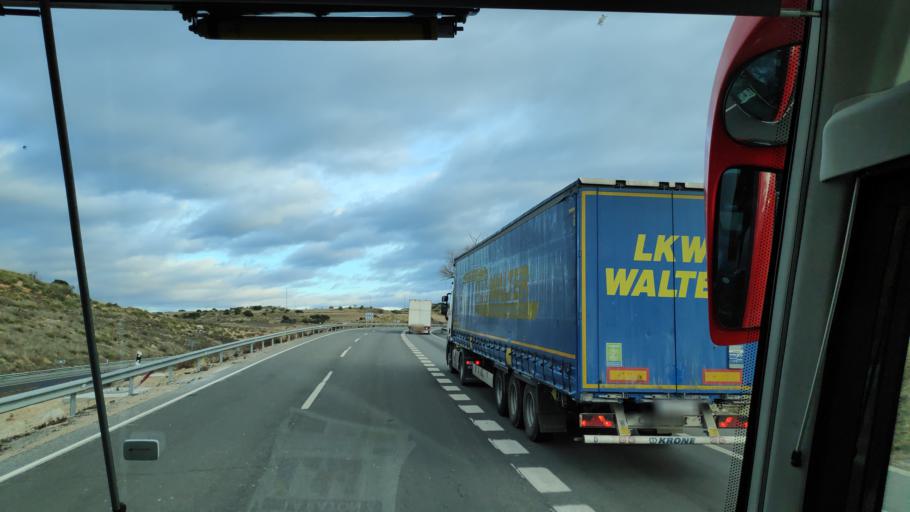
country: ES
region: Madrid
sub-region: Provincia de Madrid
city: Villarejo de Salvanes
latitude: 40.1978
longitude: -3.3093
